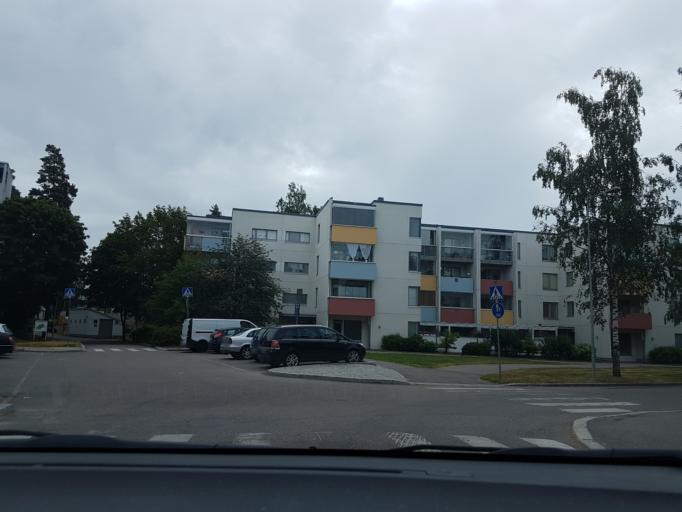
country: FI
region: Uusimaa
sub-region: Helsinki
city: Vantaa
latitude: 60.2326
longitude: 25.0579
